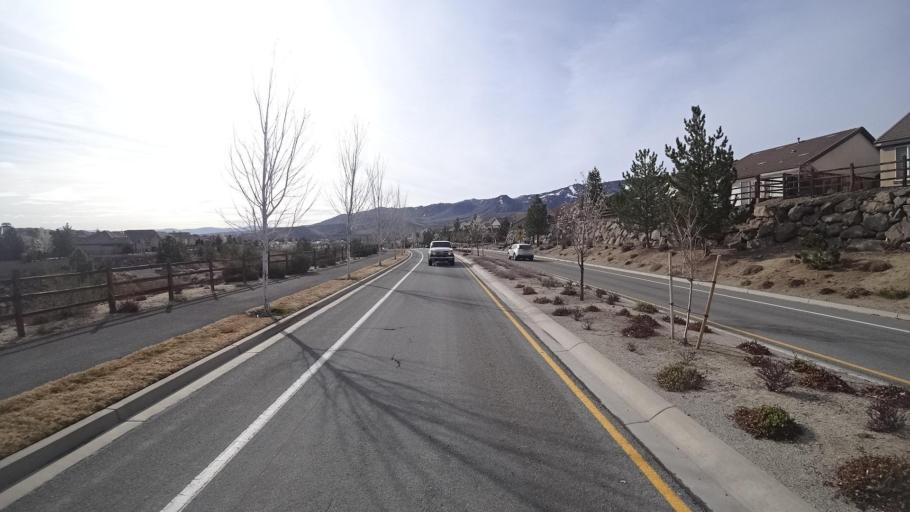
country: US
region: Nevada
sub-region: Washoe County
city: Mogul
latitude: 39.5209
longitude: -119.9480
